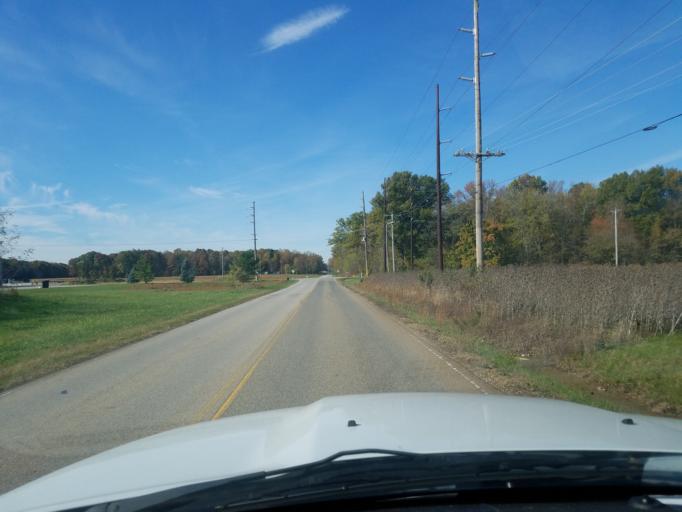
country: US
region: Indiana
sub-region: Jennings County
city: North Vernon
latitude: 39.0365
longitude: -85.6255
